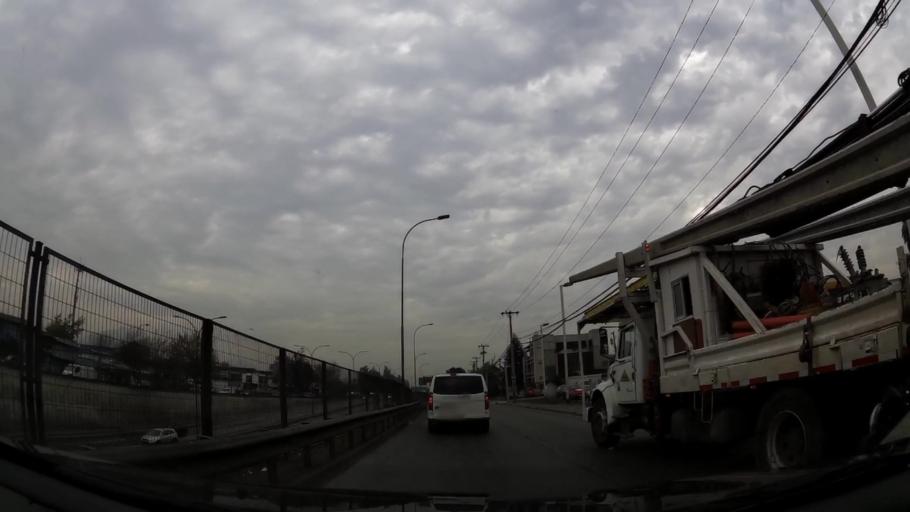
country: CL
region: Santiago Metropolitan
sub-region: Provincia de Santiago
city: Santiago
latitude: -33.4135
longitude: -70.6791
